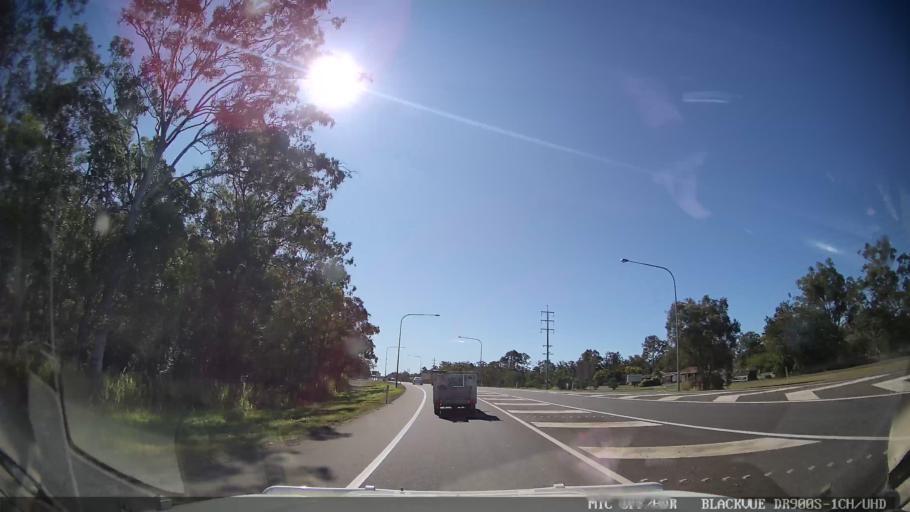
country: AU
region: Queensland
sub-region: Fraser Coast
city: Maryborough
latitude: -25.5130
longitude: 152.6708
